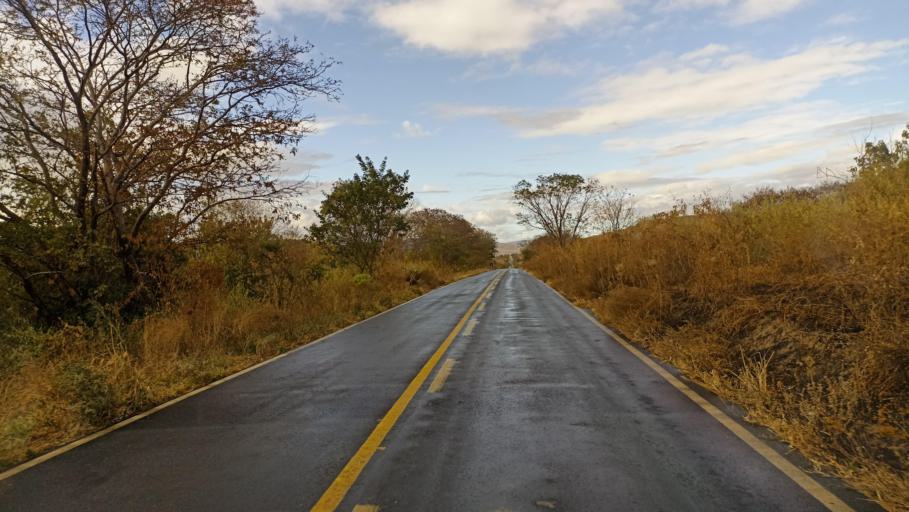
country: BR
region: Minas Gerais
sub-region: Itinga
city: Itinga
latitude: -16.5904
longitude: -41.6823
